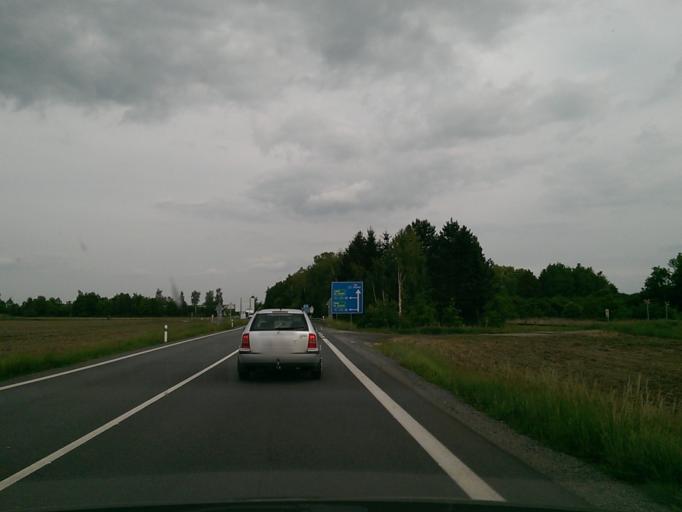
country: CZ
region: Central Bohemia
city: Bakov nad Jizerou
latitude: 50.4832
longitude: 14.9595
